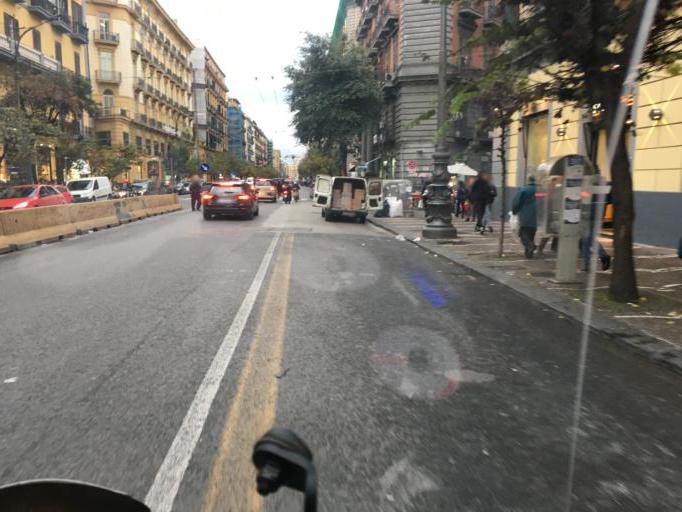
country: IT
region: Campania
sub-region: Provincia di Napoli
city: Napoli
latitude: 40.8505
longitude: 14.2660
